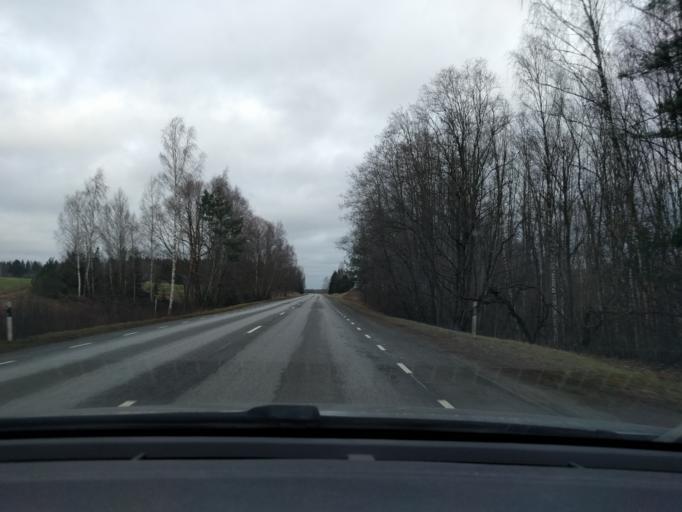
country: EE
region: Viljandimaa
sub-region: Vohma linn
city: Vohma
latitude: 58.5334
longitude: 25.5908
